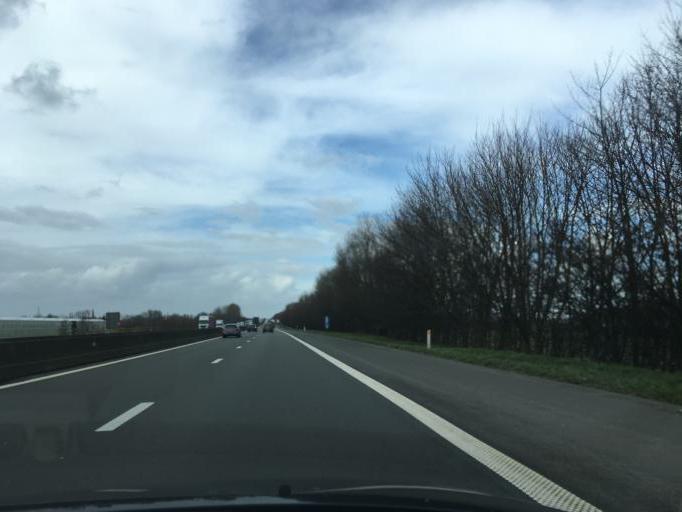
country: BE
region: Flanders
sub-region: Provincie West-Vlaanderen
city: Ardooie
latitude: 50.9816
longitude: 3.1778
